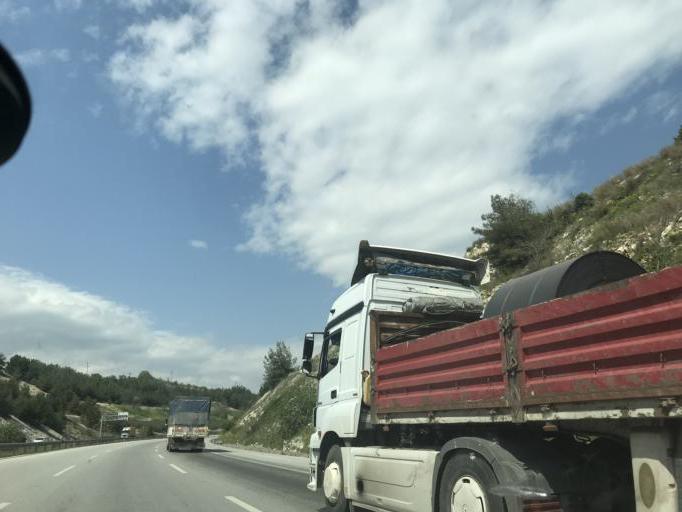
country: TR
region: Mersin
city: Camliyayla
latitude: 37.1544
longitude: 34.8394
